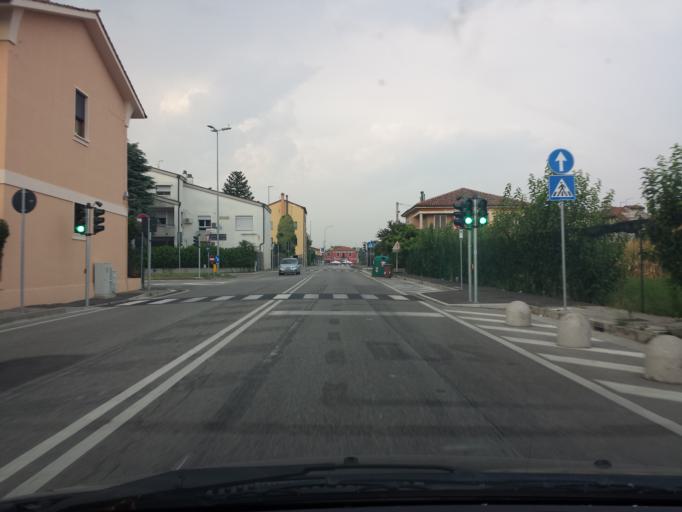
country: IT
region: Veneto
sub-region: Provincia di Vicenza
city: Vicenza
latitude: 45.5758
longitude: 11.5510
